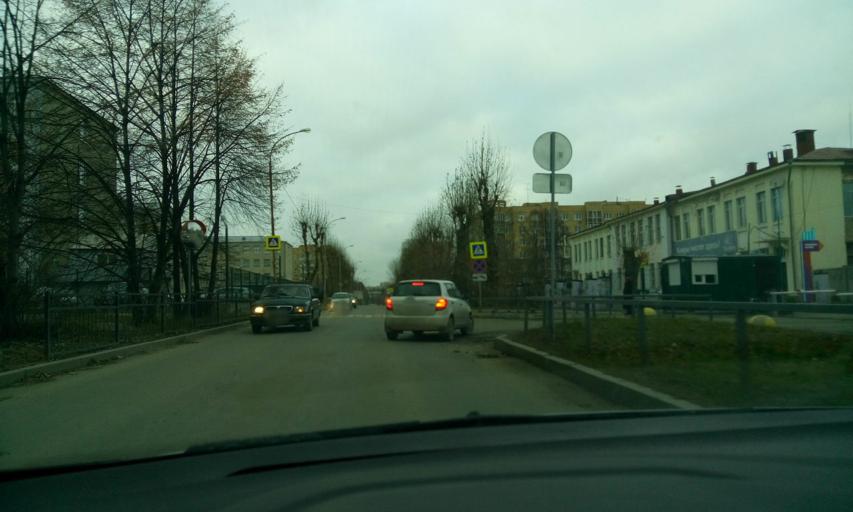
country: RU
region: Sverdlovsk
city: Yekaterinburg
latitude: 56.8429
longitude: 60.6559
